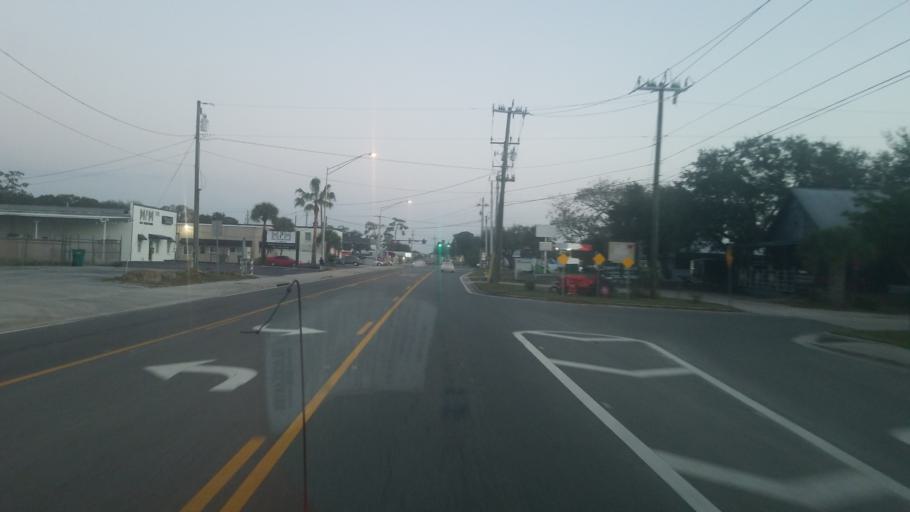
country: US
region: Florida
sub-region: Sarasota County
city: Fruitville
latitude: 27.3252
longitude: -82.4514
